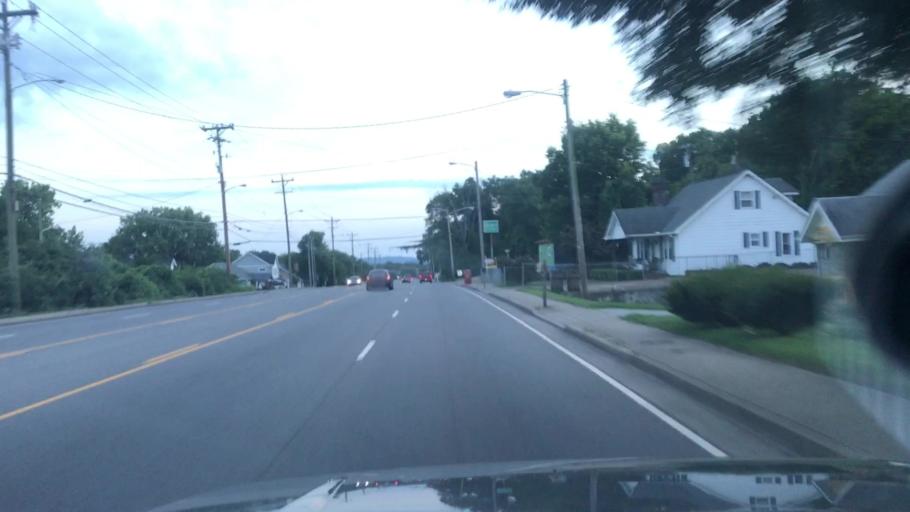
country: US
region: Tennessee
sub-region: Davidson County
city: Nashville
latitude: 36.1978
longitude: -86.8275
